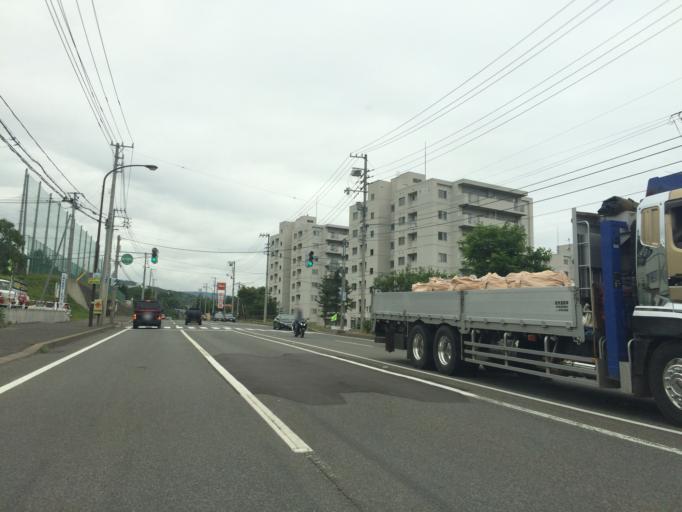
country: JP
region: Hokkaido
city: Otaru
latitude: 43.1398
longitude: 141.1572
